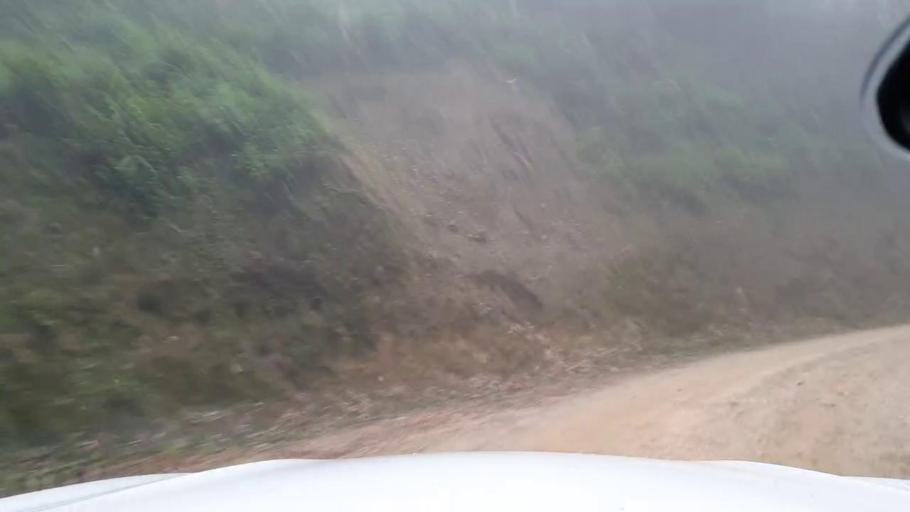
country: BI
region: Cibitoke
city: Cibitoke
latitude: -2.5929
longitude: 29.1941
